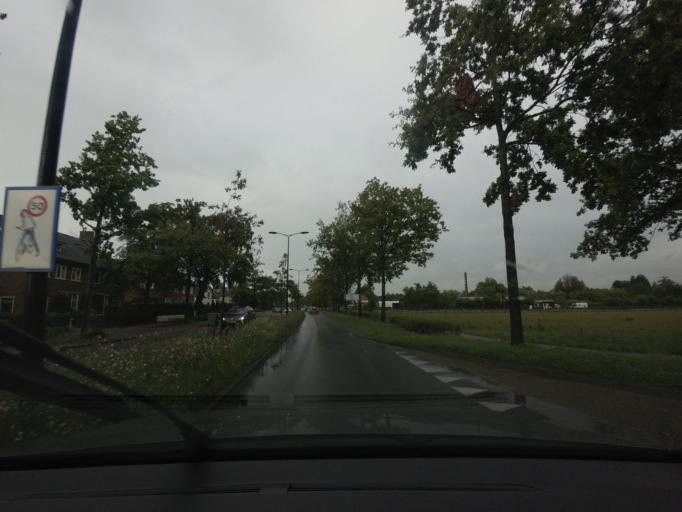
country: NL
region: South Holland
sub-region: Gemeente Voorschoten
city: Voorschoten
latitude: 52.1136
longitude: 4.4326
